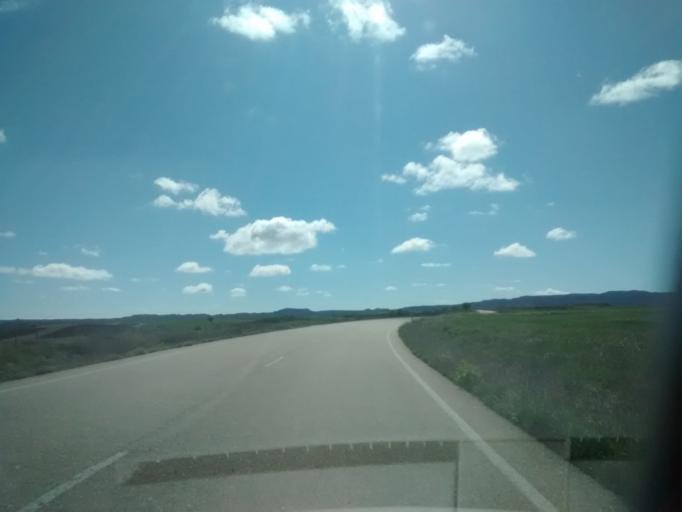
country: ES
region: Aragon
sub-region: Provincia de Zaragoza
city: Lecinena
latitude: 41.7956
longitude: -0.6462
